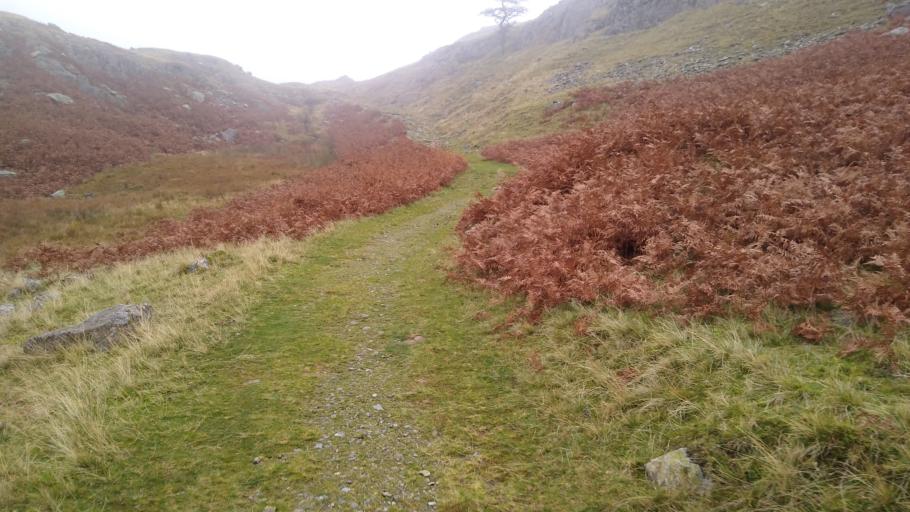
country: GB
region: England
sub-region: Cumbria
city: Ambleside
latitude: 54.4008
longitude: -3.0821
